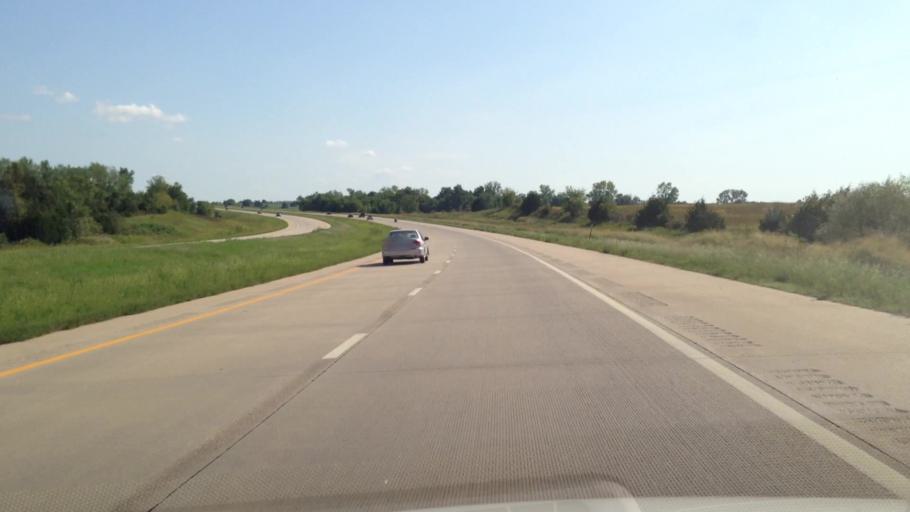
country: US
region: Kansas
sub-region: Bourbon County
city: Fort Scott
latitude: 37.9642
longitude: -94.7084
